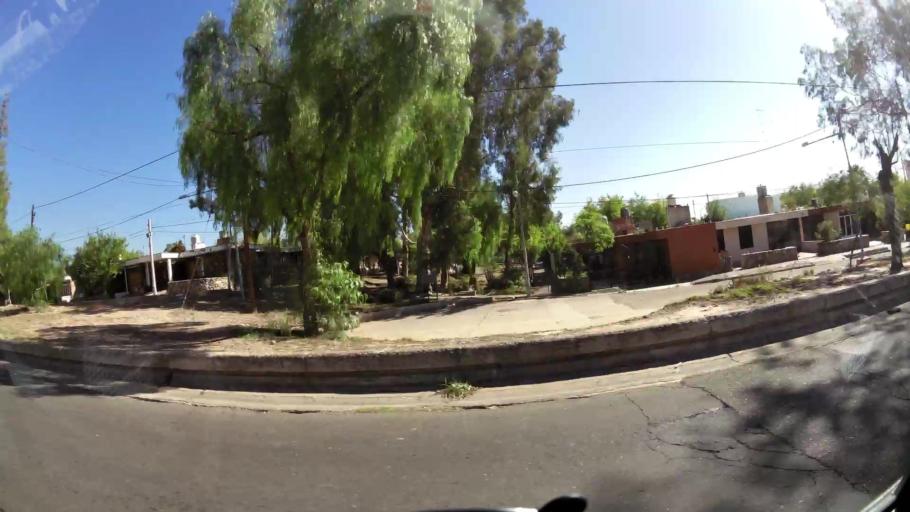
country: AR
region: Mendoza
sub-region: Departamento de Godoy Cruz
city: Godoy Cruz
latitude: -32.9042
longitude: -68.8843
